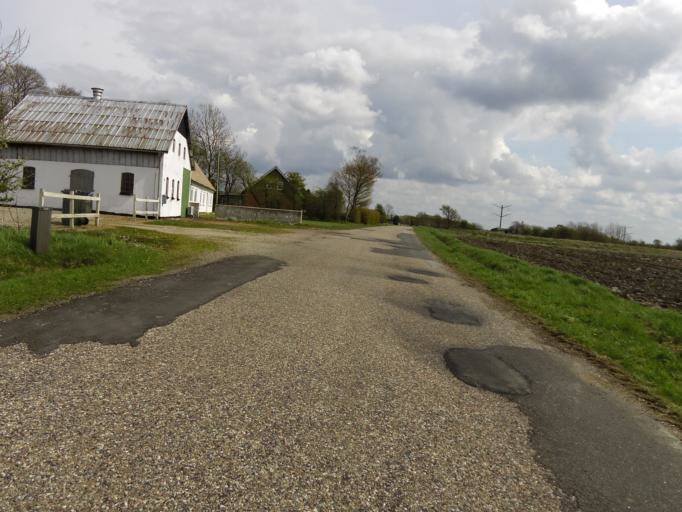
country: DK
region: South Denmark
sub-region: Tonder Kommune
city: Toftlund
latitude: 55.2108
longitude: 9.1440
